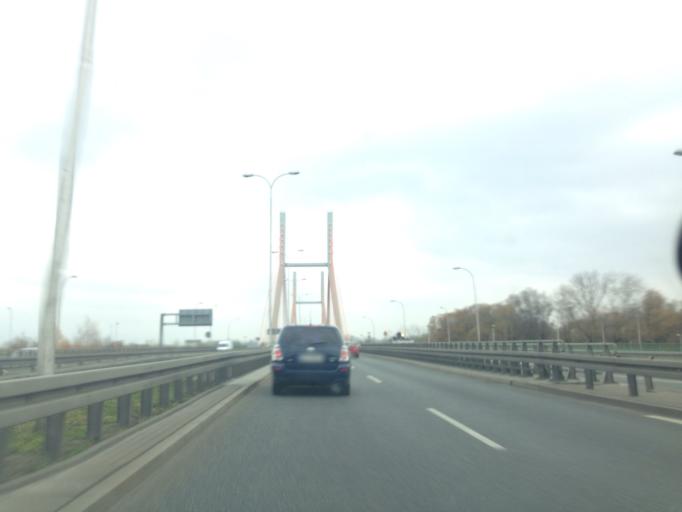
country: PL
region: Masovian Voivodeship
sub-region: Warszawa
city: Praga Poludnie
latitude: 52.2180
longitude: 21.0980
